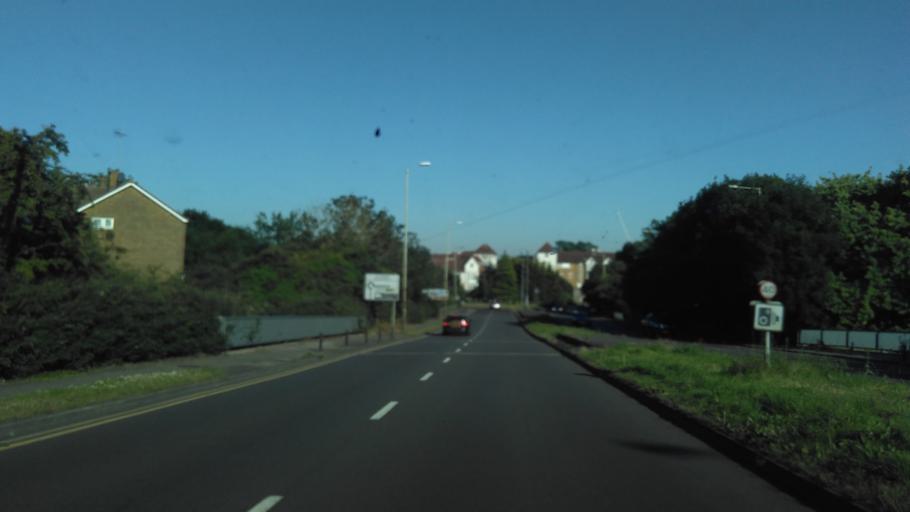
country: GB
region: England
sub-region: Kent
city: Canterbury
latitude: 51.2799
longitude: 1.0709
